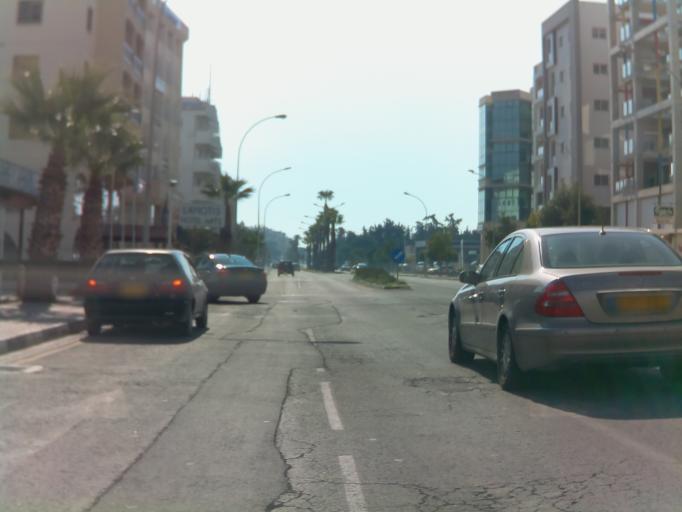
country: CY
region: Larnaka
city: Larnaca
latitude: 34.9090
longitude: 33.6295
